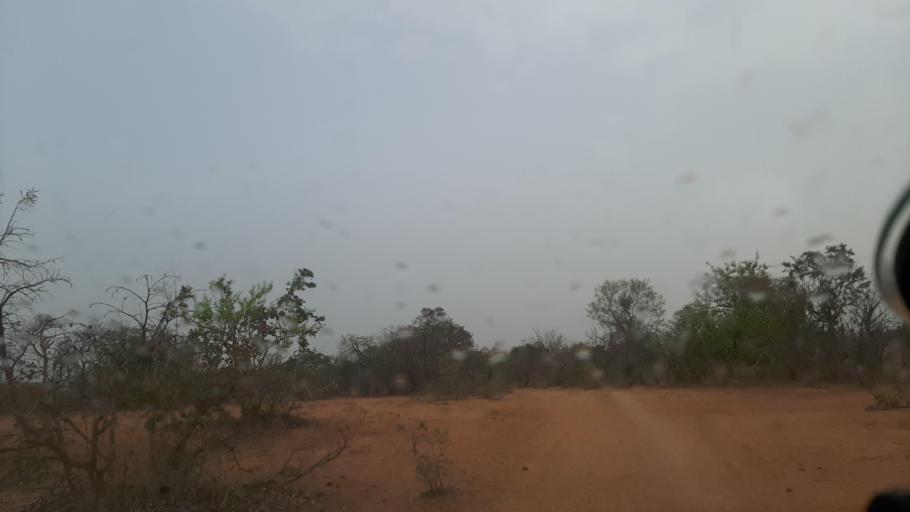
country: BF
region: Boucle du Mouhoun
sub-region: Province des Banwa
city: Salanso
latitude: 11.8637
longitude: -4.4402
